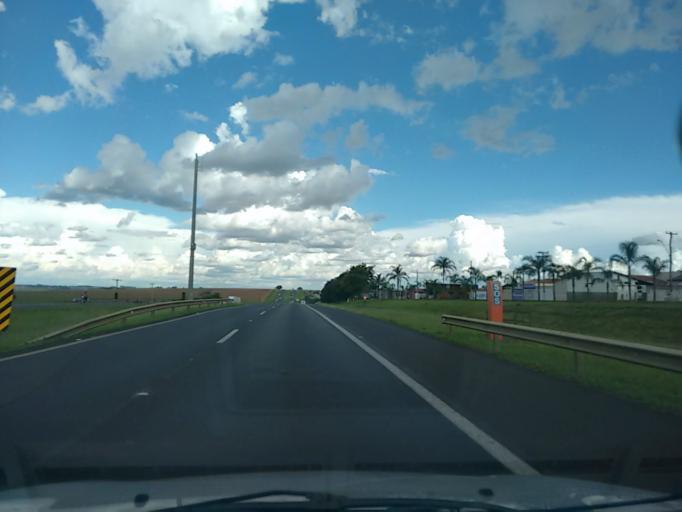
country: BR
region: Sao Paulo
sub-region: Ibate
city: Ibate
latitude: -21.9508
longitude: -47.9927
